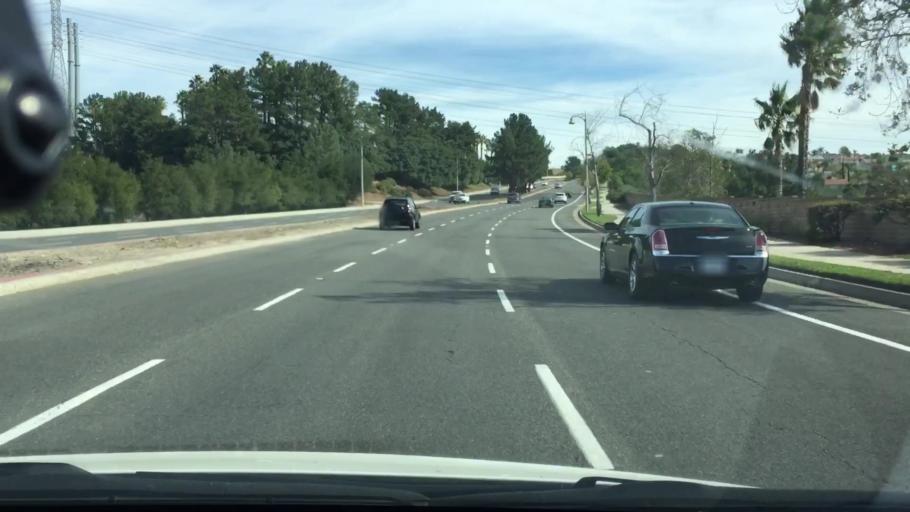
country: US
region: California
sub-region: Orange County
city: Portola Hills
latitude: 33.6509
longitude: -117.6386
